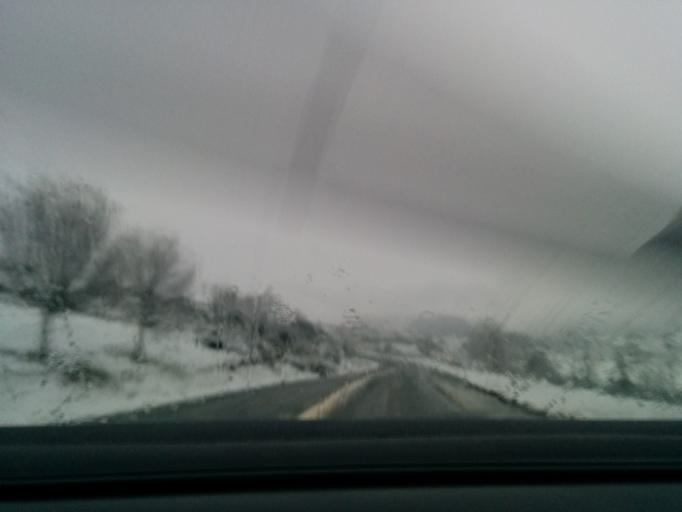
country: ES
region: Navarre
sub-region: Provincia de Navarra
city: Egues-Uharte
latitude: 42.7908
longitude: -1.5525
